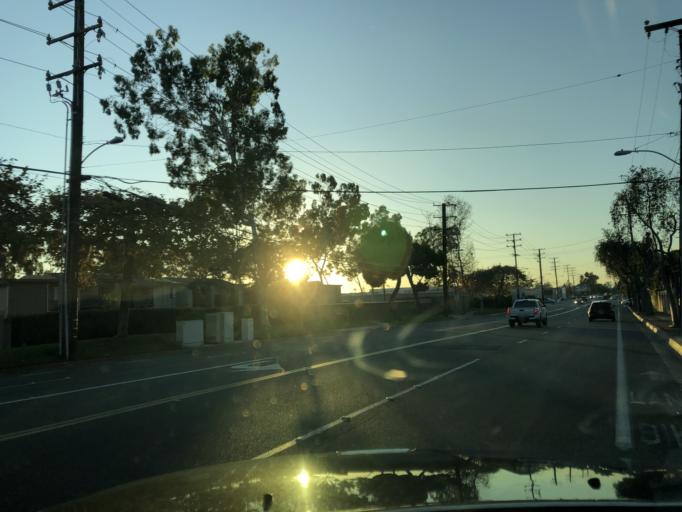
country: US
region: California
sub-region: Orange County
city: Costa Mesa
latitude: 33.6824
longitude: -117.8804
